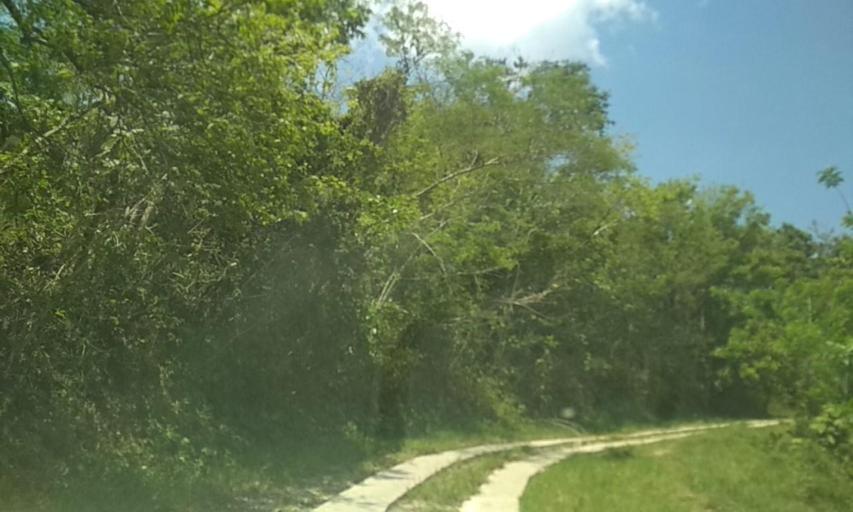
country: MX
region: Chiapas
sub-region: Tecpatan
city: Raudales Malpaso
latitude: 17.3017
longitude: -93.8273
